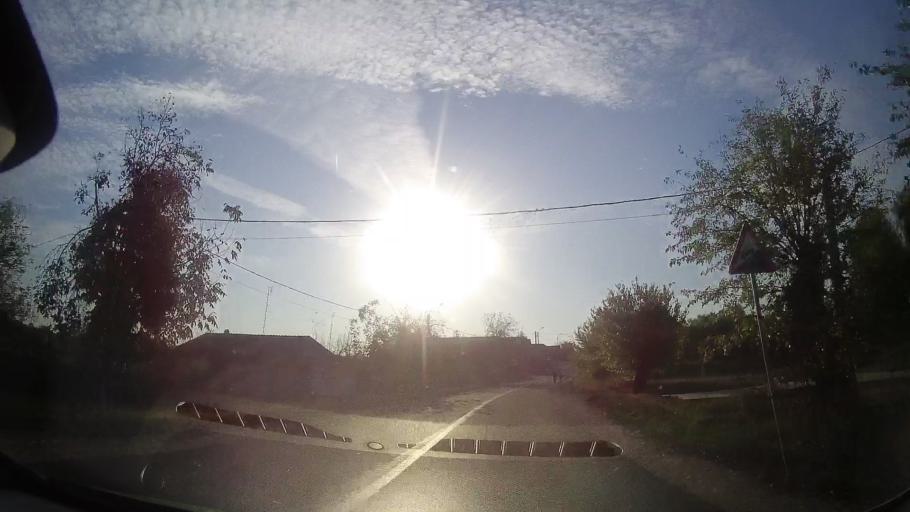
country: RO
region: Timis
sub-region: Comuna Masloc
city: Masloc
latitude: 45.9694
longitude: 21.4762
